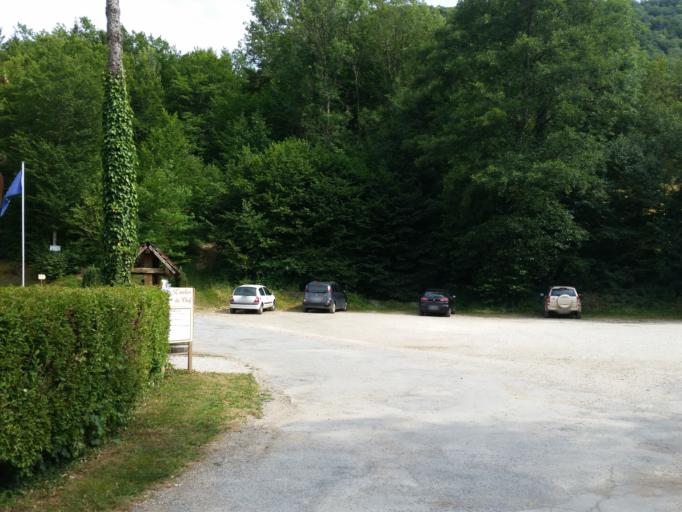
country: FR
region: Franche-Comte
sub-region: Departement du Jura
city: Salins-les-Bains
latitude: 46.9728
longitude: 5.9971
